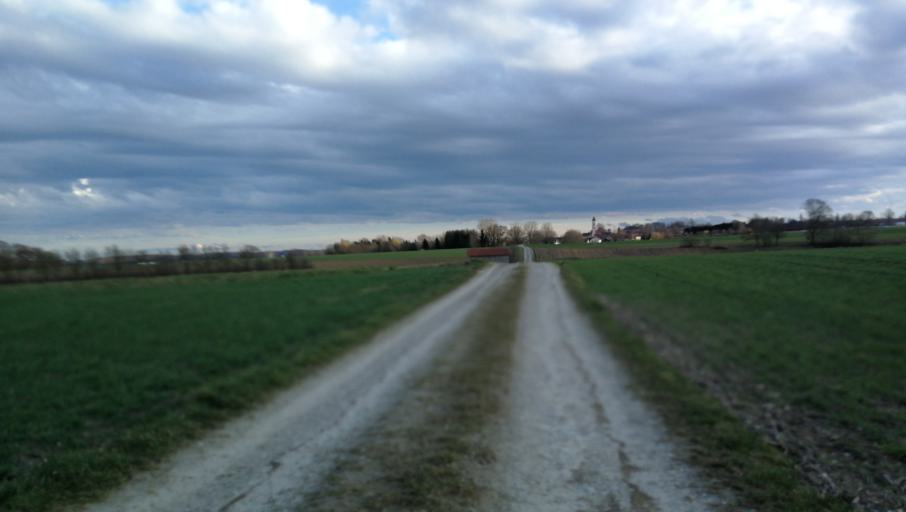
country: DE
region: Bavaria
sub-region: Upper Bavaria
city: Fuerstenfeldbruck
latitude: 48.1988
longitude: 11.2177
